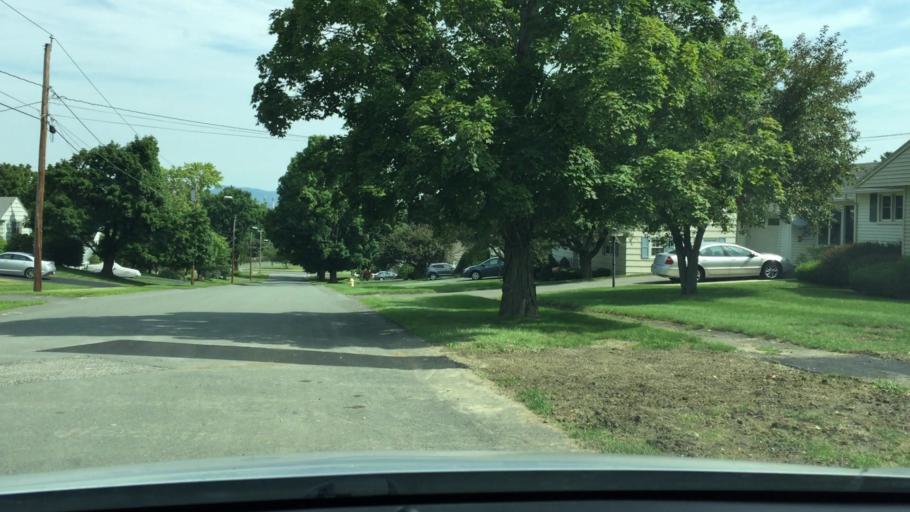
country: US
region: Massachusetts
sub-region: Berkshire County
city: Pittsfield
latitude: 42.4351
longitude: -73.2228
